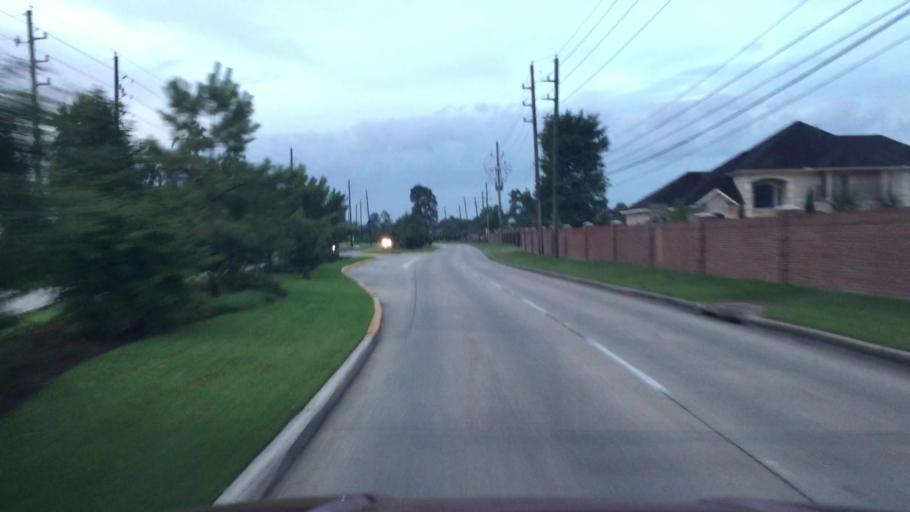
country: US
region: Texas
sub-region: Harris County
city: Tomball
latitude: 30.0368
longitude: -95.5363
